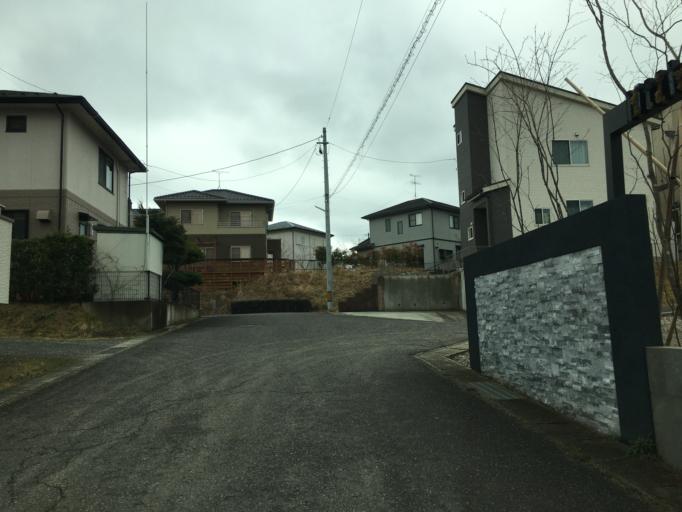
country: JP
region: Fukushima
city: Fukushima-shi
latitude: 37.7170
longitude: 140.4062
